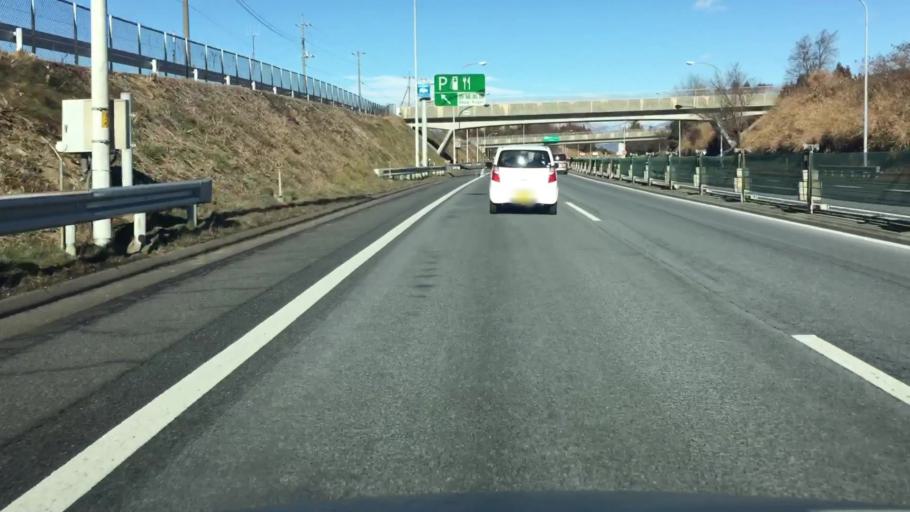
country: JP
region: Gunma
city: Numata
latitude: 36.5984
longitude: 139.0637
